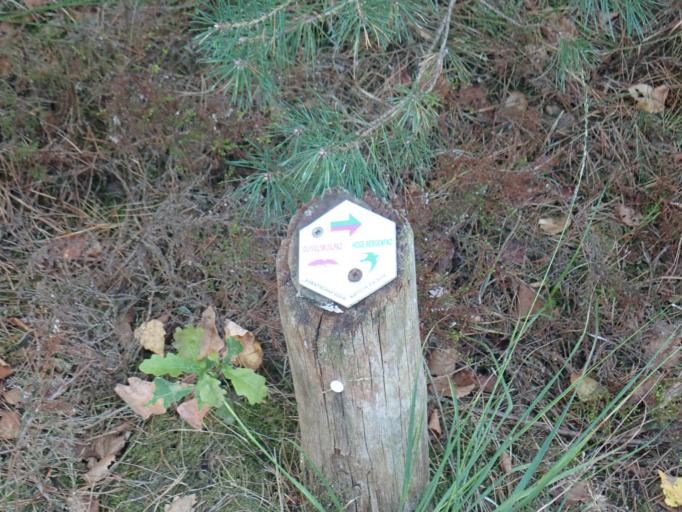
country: BE
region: Flanders
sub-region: Provincie Antwerpen
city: Rijkevorsel
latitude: 51.3154
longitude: 4.7985
